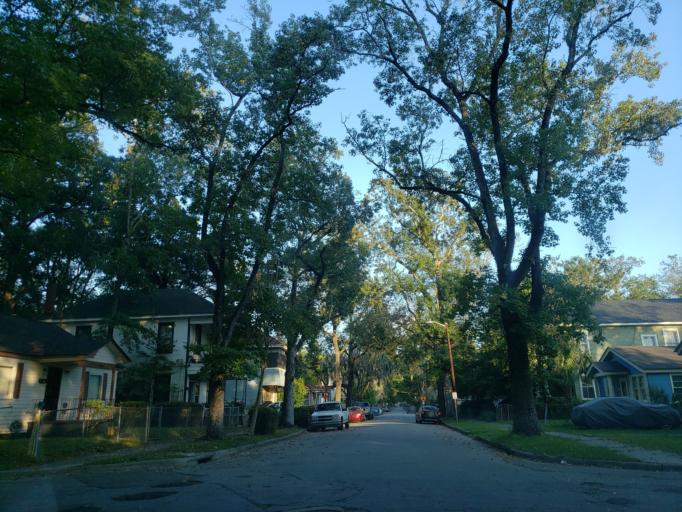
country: US
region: Georgia
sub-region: Chatham County
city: Savannah
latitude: 32.0562
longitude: -81.0893
